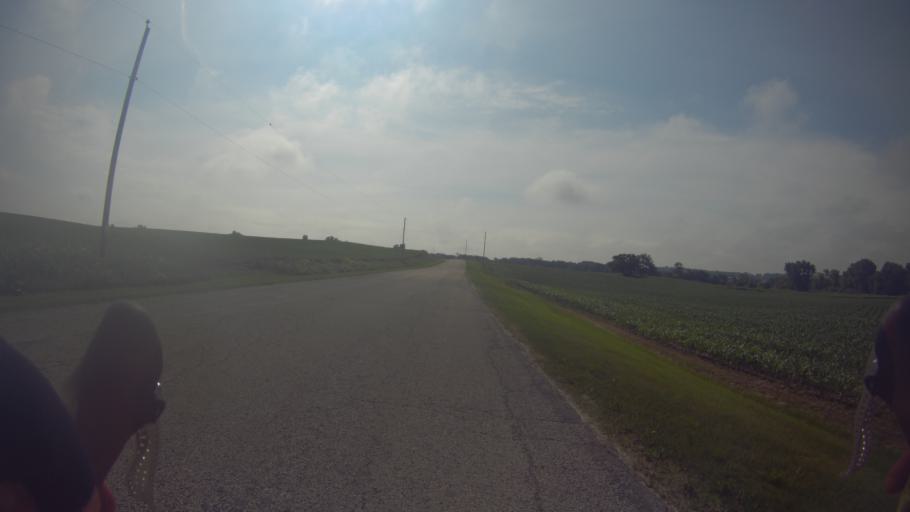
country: US
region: Wisconsin
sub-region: Dane County
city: Stoughton
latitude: 42.9807
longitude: -89.1900
